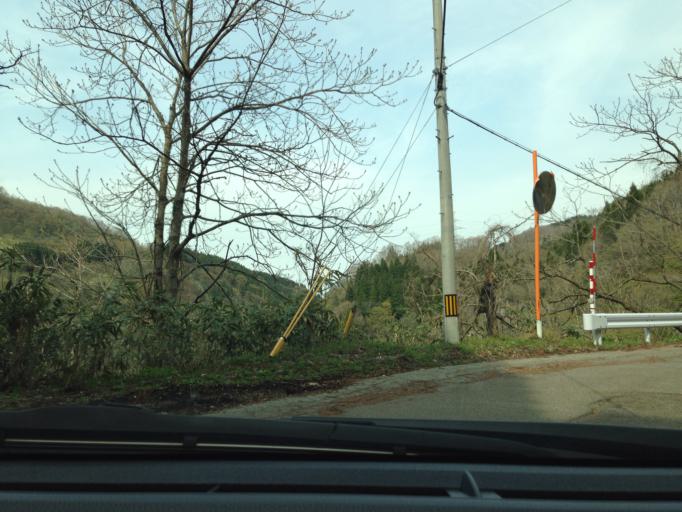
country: JP
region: Toyama
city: Fukumitsu
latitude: 36.4752
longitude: 136.8083
